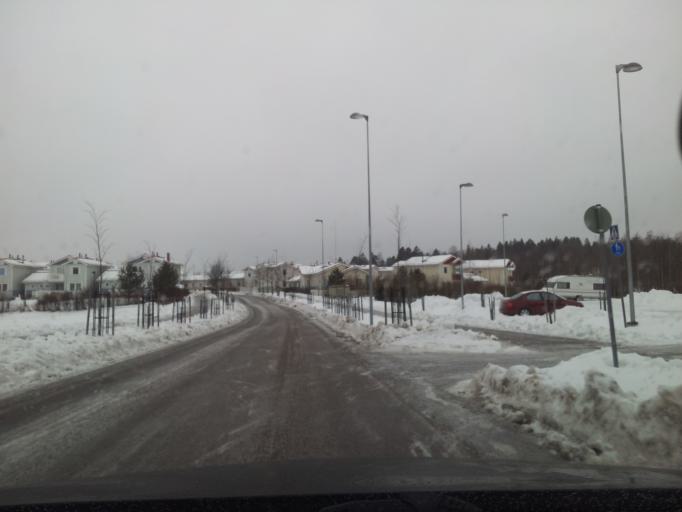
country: FI
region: Uusimaa
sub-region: Helsinki
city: Espoo
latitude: 60.1597
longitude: 24.5547
